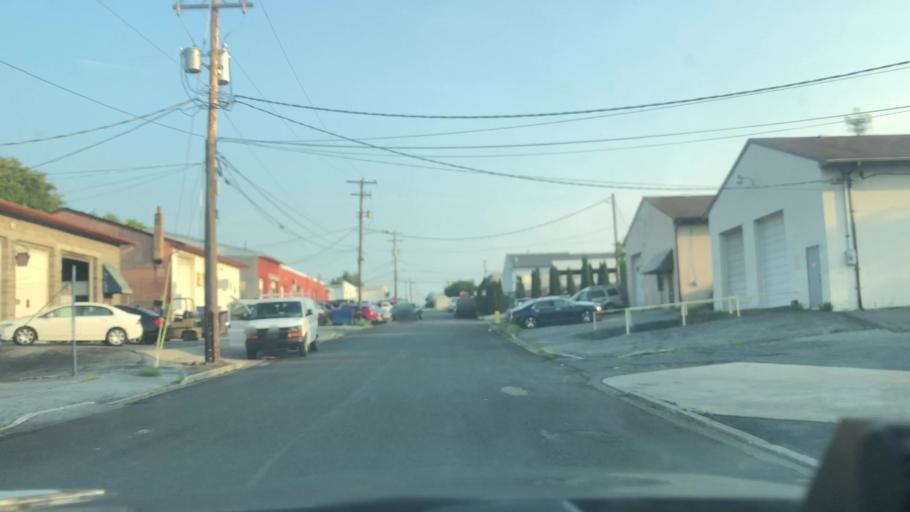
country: US
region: Pennsylvania
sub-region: Lehigh County
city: Fullerton
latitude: 40.6275
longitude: -75.4466
